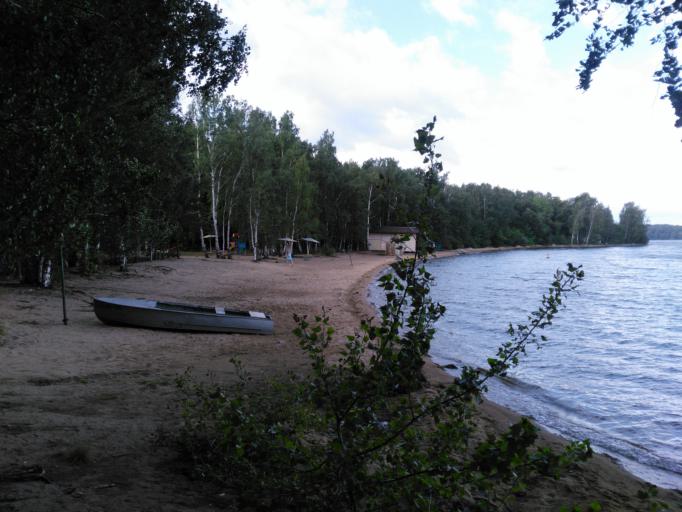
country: RU
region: Chelyabinsk
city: Tayginka
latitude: 55.4800
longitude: 60.4978
